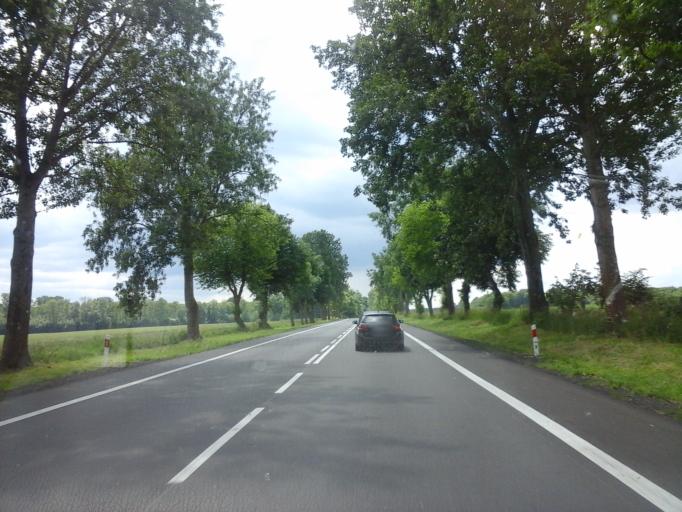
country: PL
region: West Pomeranian Voivodeship
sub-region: Powiat bialogardzki
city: Karlino
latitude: 54.0127
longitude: 15.8156
